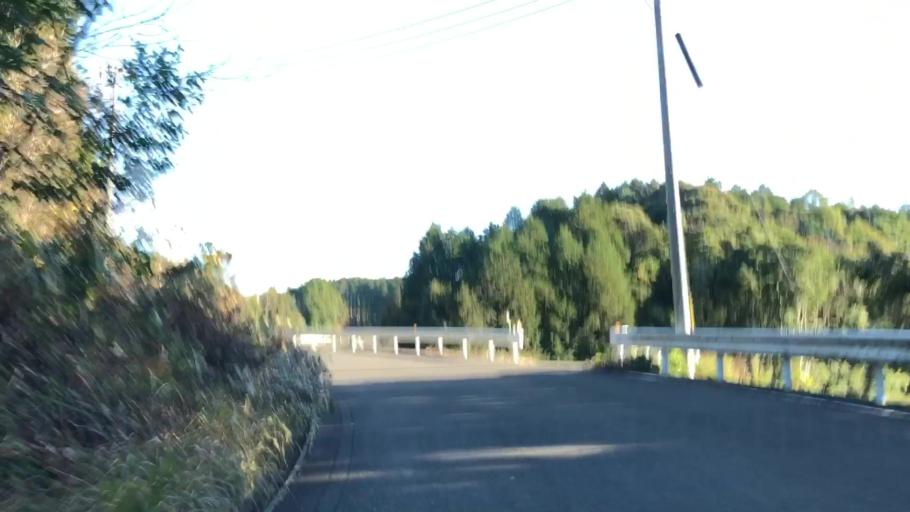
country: JP
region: Nagasaki
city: Sasebo
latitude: 33.0293
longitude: 129.6792
